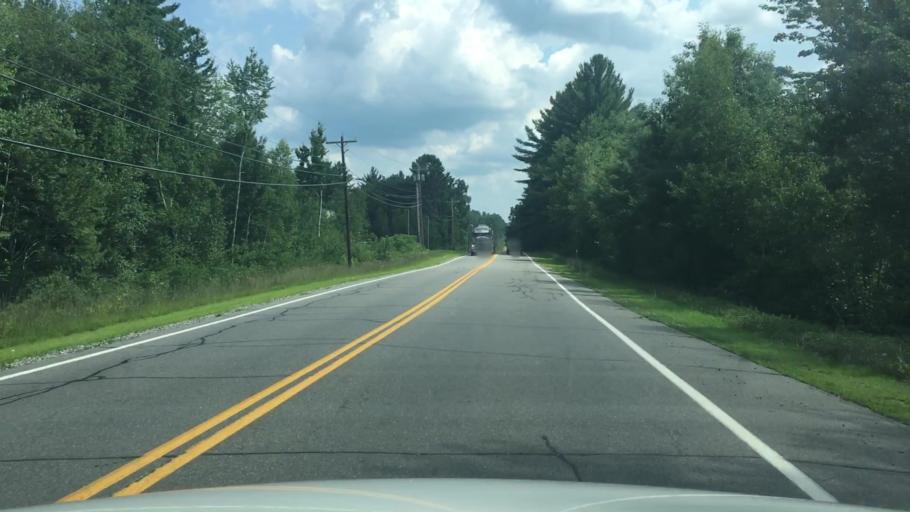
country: US
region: New Hampshire
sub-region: Rockingham County
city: Auburn
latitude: 42.9523
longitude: -71.3535
